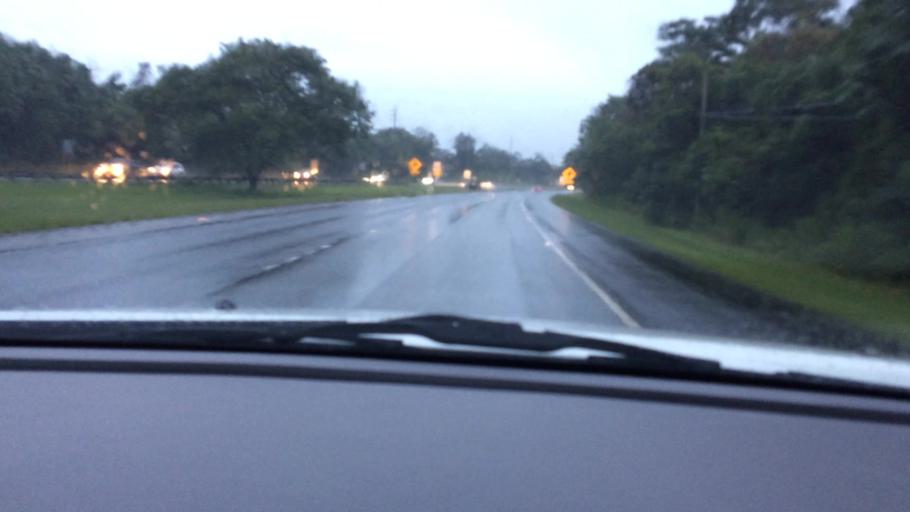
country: US
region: Hawaii
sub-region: Hawaii County
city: Kea'au
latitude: 19.6669
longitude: -155.0624
